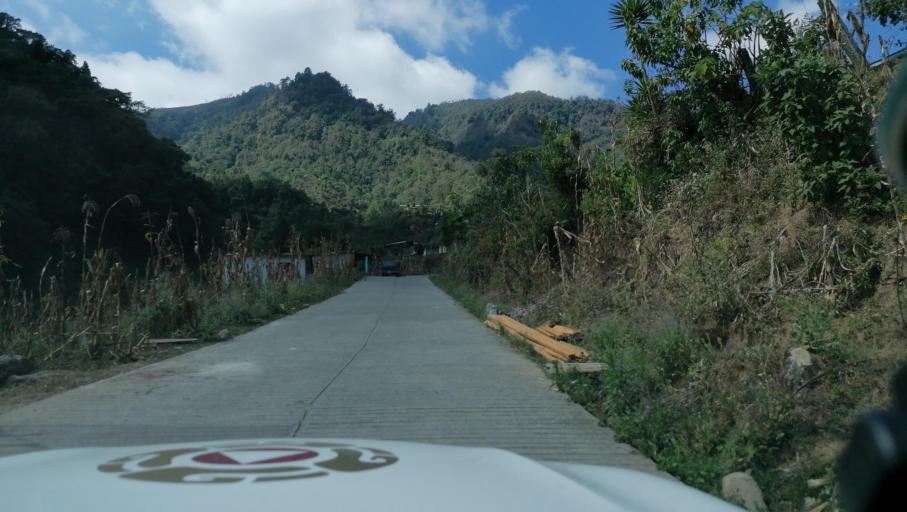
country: GT
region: San Marcos
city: Tacana
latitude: 15.2018
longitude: -92.2026
